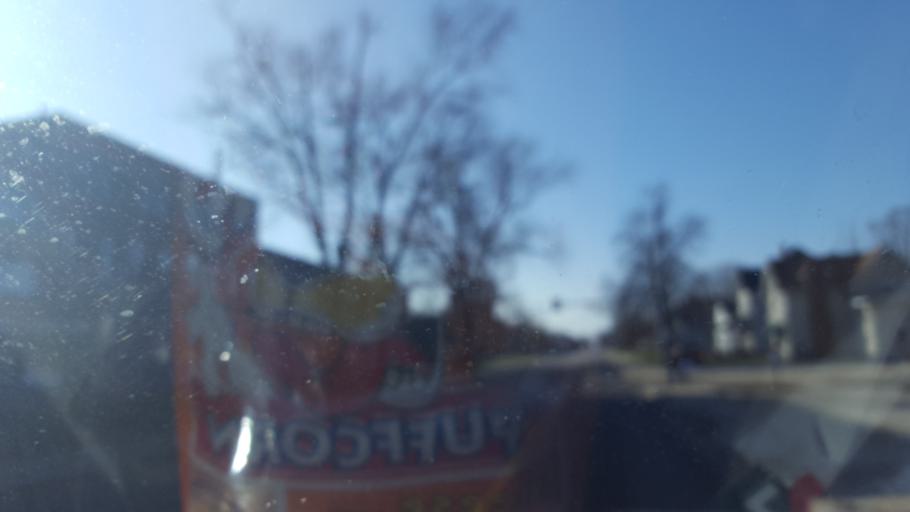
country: US
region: Indiana
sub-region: Elkhart County
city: Nappanee
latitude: 41.4426
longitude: -85.9962
